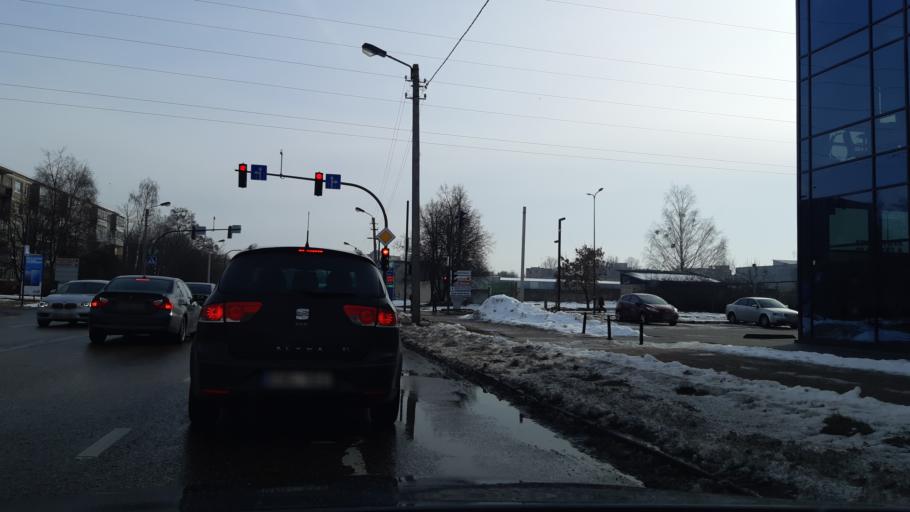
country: LT
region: Kauno apskritis
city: Dainava (Kaunas)
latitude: 54.9175
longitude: 23.9528
